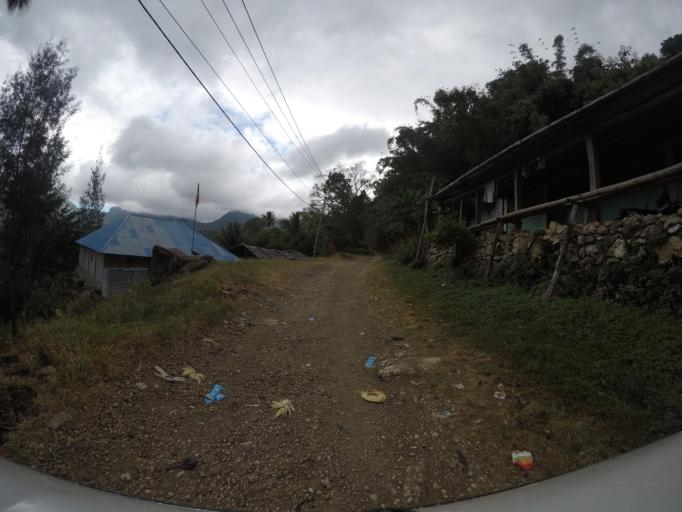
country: TL
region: Baucau
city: Baucau
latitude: -8.6440
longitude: 126.6339
